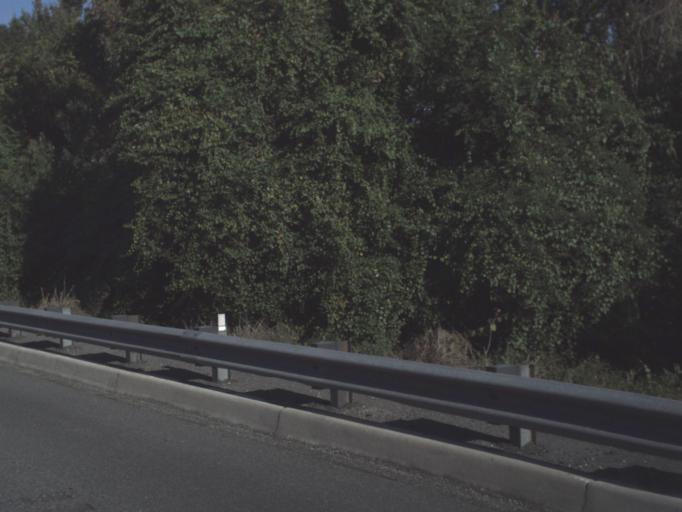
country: US
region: Florida
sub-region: Orange County
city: Oakland
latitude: 28.5552
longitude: -81.6672
